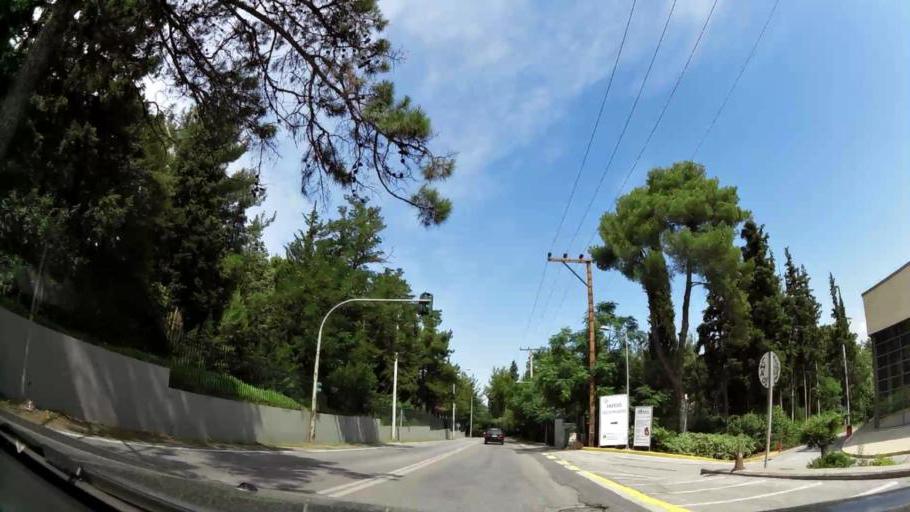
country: GR
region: Central Macedonia
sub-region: Nomos Thessalonikis
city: Pylaia
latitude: 40.5948
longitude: 23.0064
